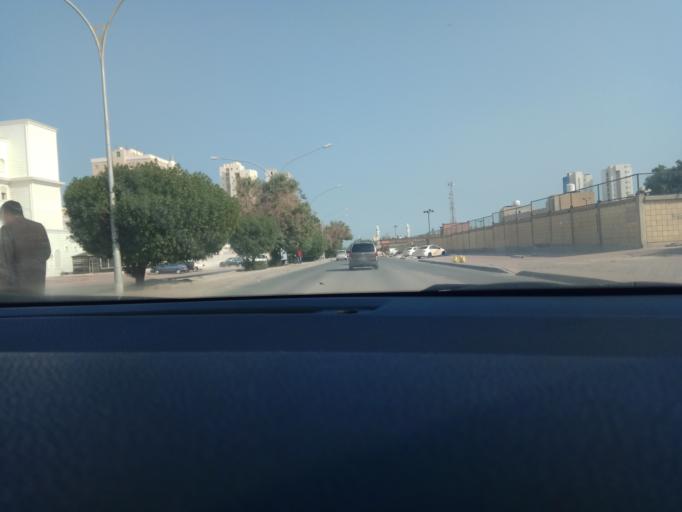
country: KW
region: Al Ahmadi
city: Al Fahahil
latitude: 29.0799
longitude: 48.1290
